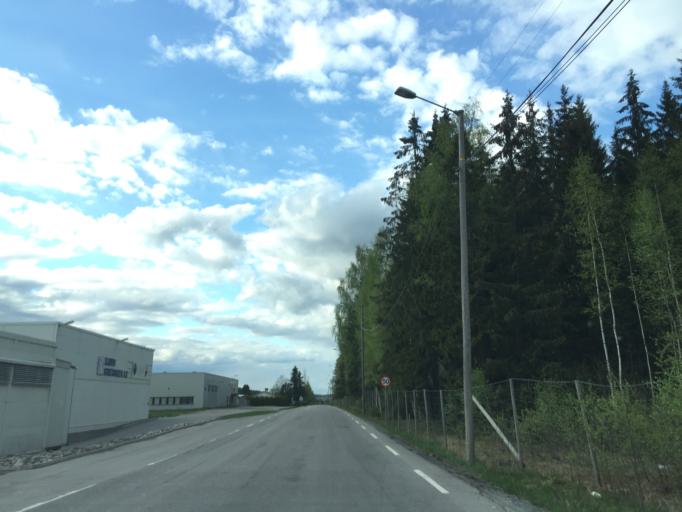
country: NO
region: Hedmark
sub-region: Kongsvinger
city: Kongsvinger
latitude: 60.1816
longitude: 12.0217
